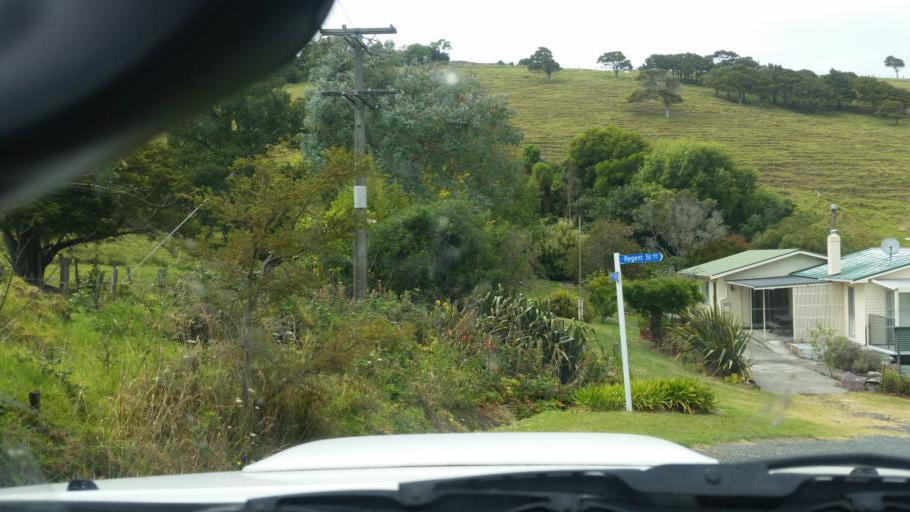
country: NZ
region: Auckland
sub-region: Auckland
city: Wellsford
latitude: -36.1576
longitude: 174.2390
